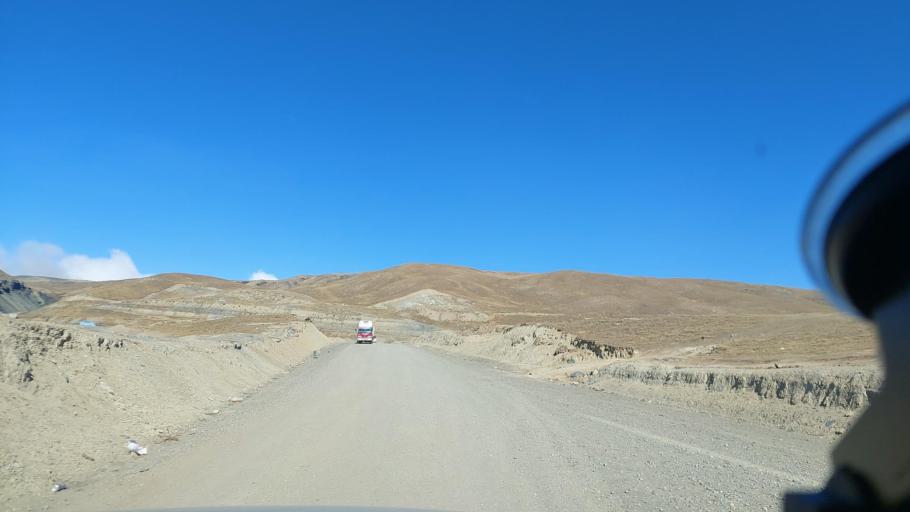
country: BO
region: La Paz
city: La Paz
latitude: -16.3452
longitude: -68.0417
